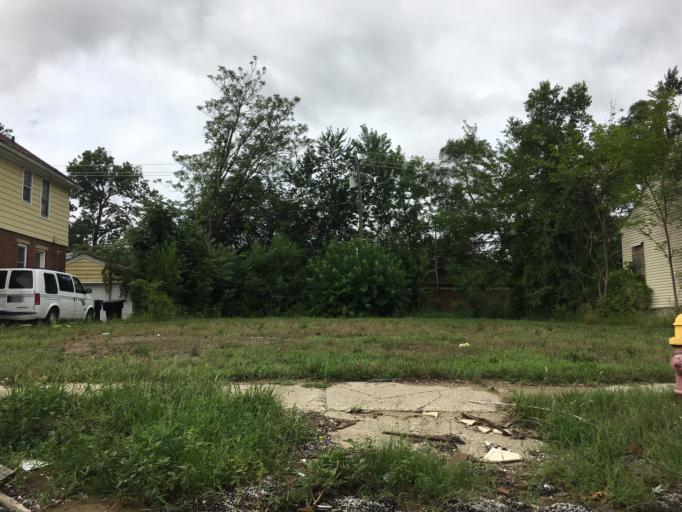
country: US
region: Michigan
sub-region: Oakland County
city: Ferndale
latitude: 42.4158
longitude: -83.1500
